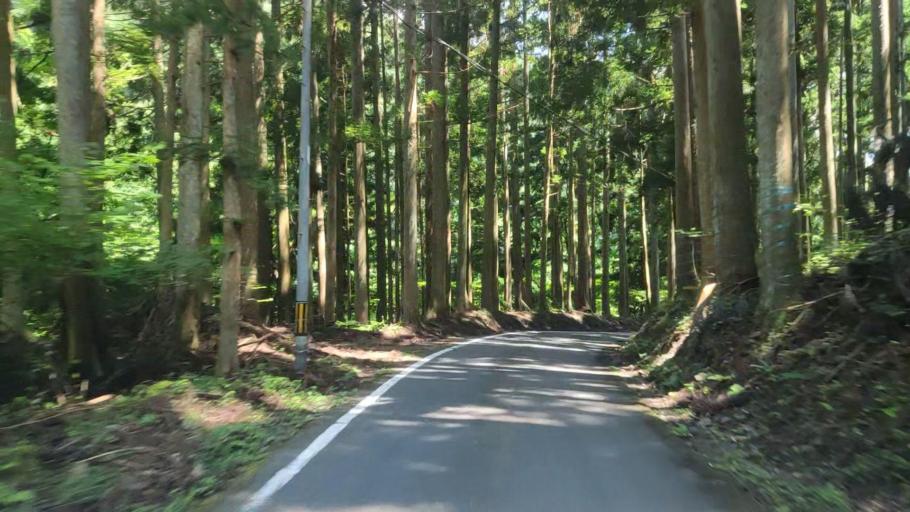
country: JP
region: Fukui
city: Ono
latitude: 35.7269
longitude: 136.5795
